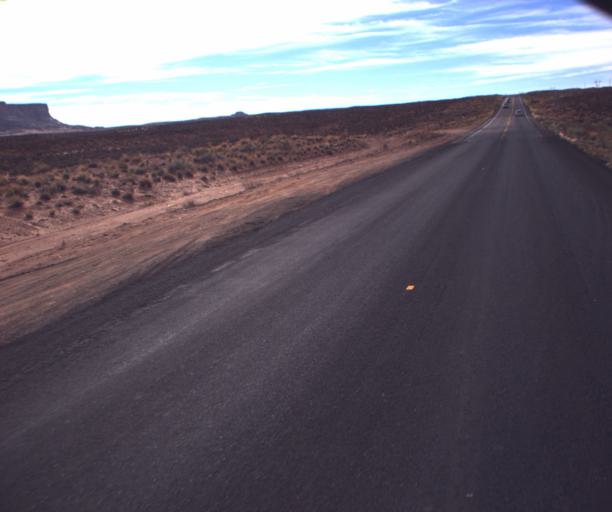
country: US
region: Arizona
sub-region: Coconino County
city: LeChee
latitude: 36.8734
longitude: -111.3425
